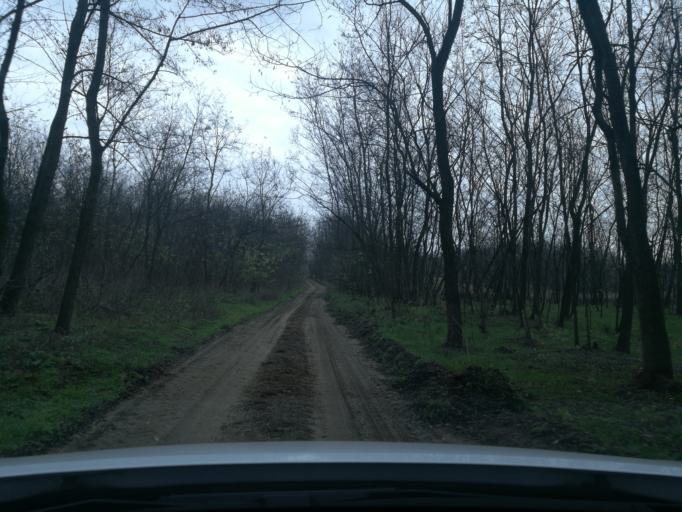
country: HU
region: Szabolcs-Szatmar-Bereg
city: Nyirpazony
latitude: 47.9700
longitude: 21.7887
